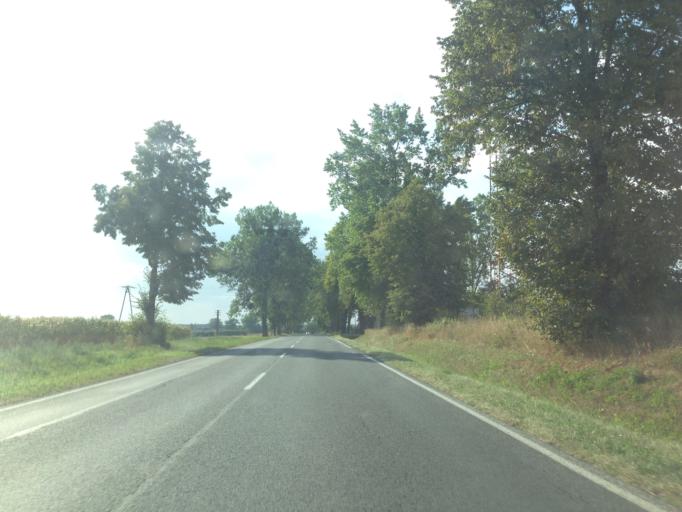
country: PL
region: Kujawsko-Pomorskie
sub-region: Powiat swiecki
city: Bukowiec
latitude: 53.4535
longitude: 18.2119
